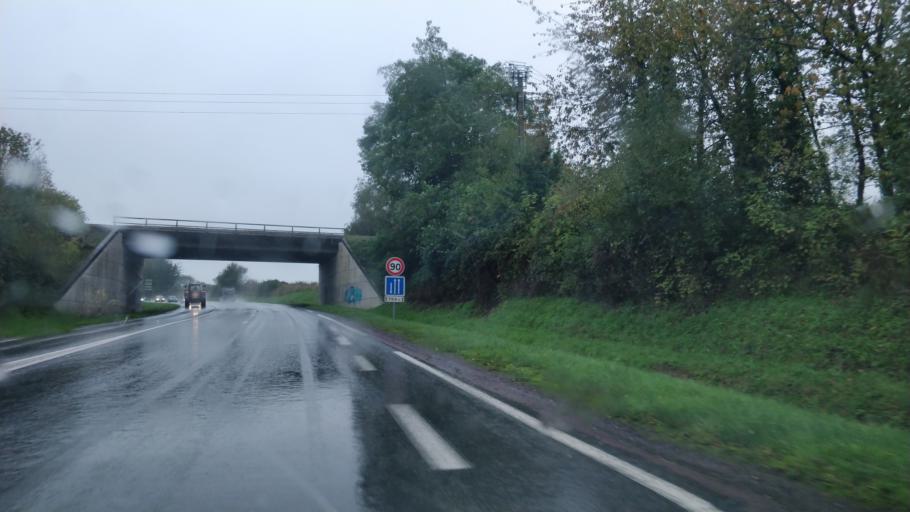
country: FR
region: Lower Normandy
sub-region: Departement de la Manche
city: Saint-Planchers
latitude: 48.8492
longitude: -1.5418
